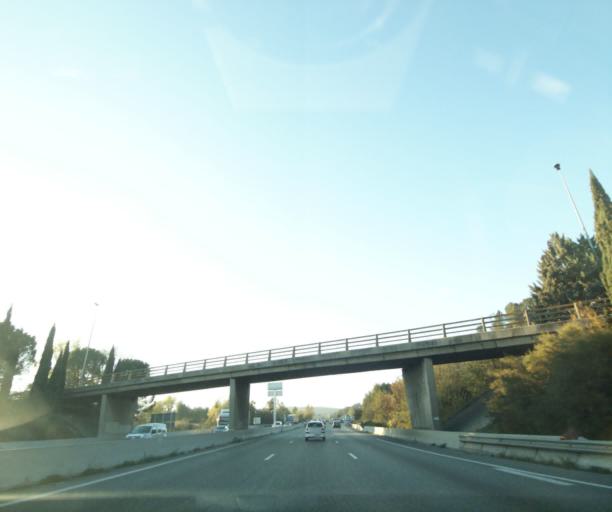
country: FR
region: Provence-Alpes-Cote d'Azur
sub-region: Departement des Bouches-du-Rhone
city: Chateauneuf-le-Rouge
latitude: 43.4845
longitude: 5.5361
